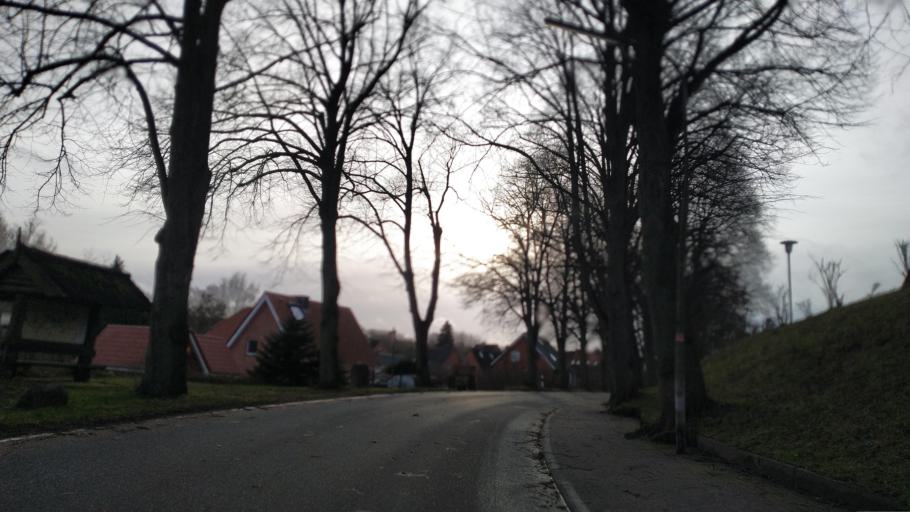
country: DE
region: Schleswig-Holstein
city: Neukirchen
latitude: 54.2064
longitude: 10.5887
